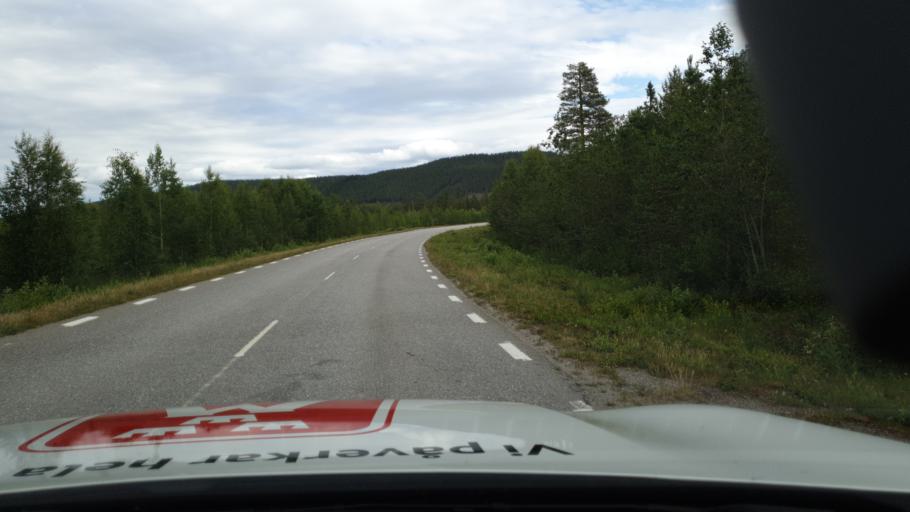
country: SE
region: Vaesterbotten
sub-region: Sorsele Kommun
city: Sorsele
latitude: 65.5403
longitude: 17.3988
